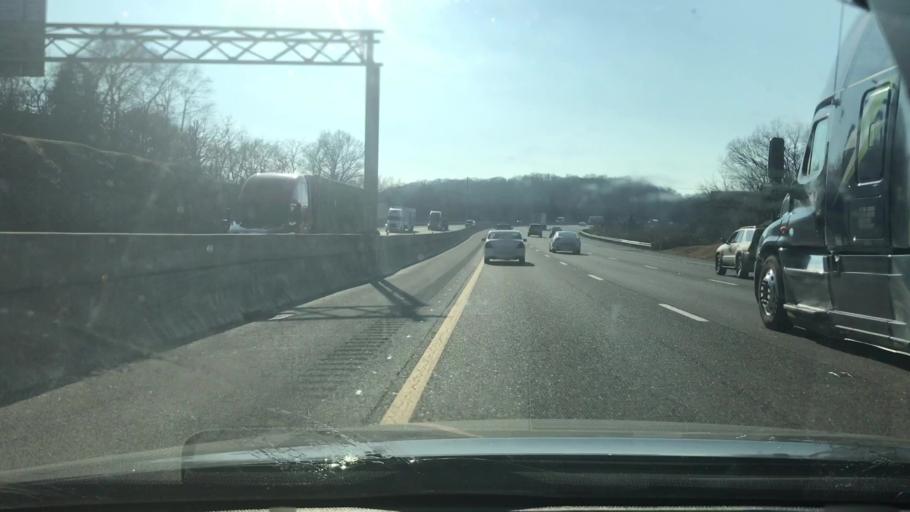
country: US
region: Tennessee
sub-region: Davidson County
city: Belle Meade
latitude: 36.1289
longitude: -86.9004
